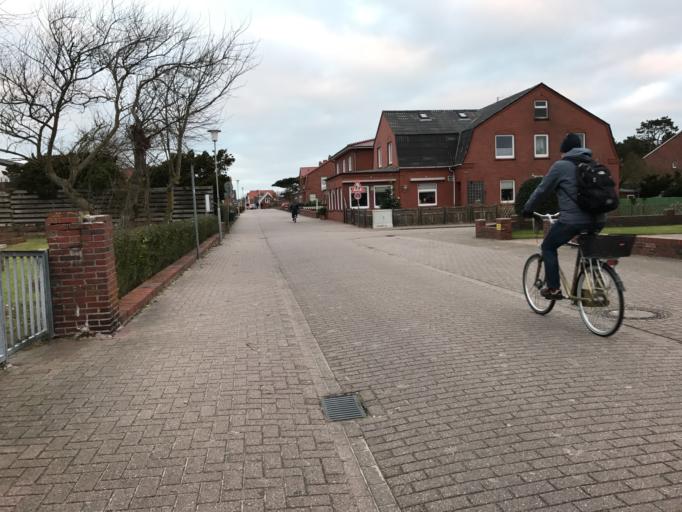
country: DE
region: Lower Saxony
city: Borkum
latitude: 53.5806
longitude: 6.6670
